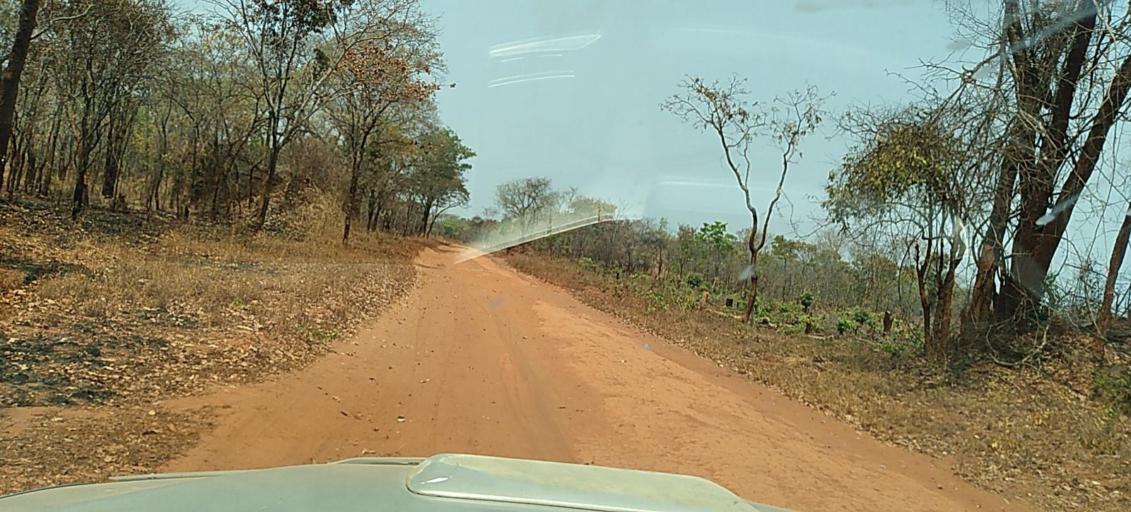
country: ZM
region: North-Western
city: Kasempa
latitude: -13.6232
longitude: 26.2082
